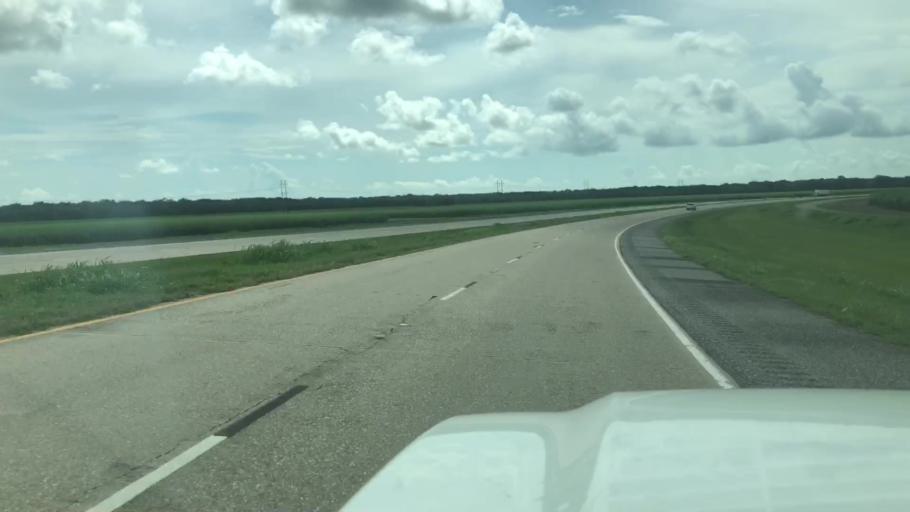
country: US
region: Louisiana
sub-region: Saint Mary Parish
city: Franklin
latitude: 29.7576
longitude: -91.4694
